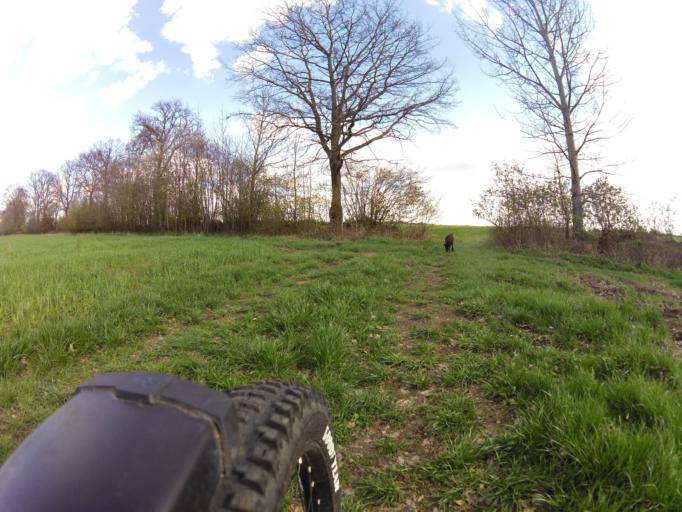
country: PL
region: West Pomeranian Voivodeship
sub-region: Powiat gryficki
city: Ploty
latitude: 53.8309
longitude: 15.2586
